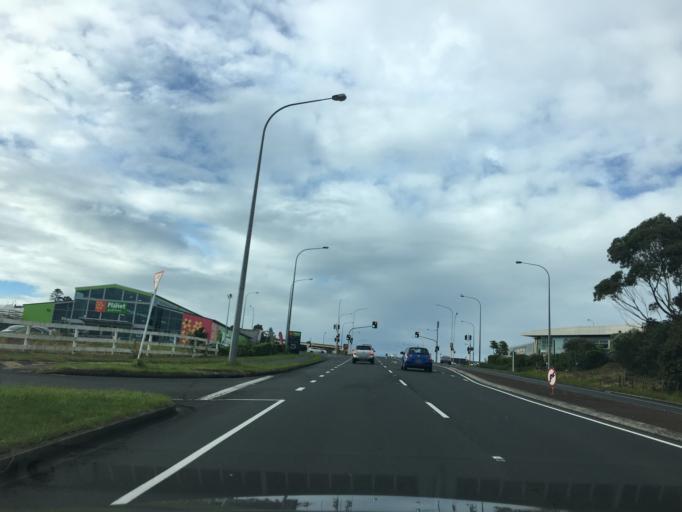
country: NZ
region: Auckland
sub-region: Auckland
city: Rothesay Bay
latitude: -36.7317
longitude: 174.7219
